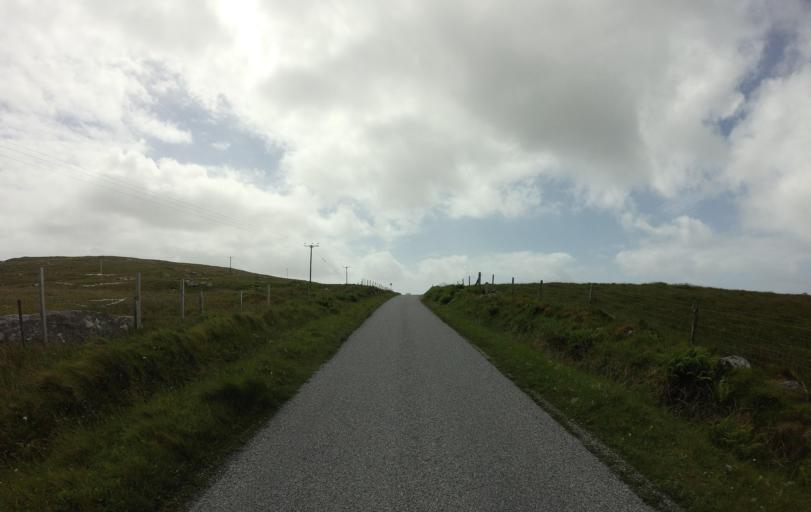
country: GB
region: Scotland
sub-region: Eilean Siar
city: Isle of South Uist
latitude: 57.1481
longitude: -7.3720
